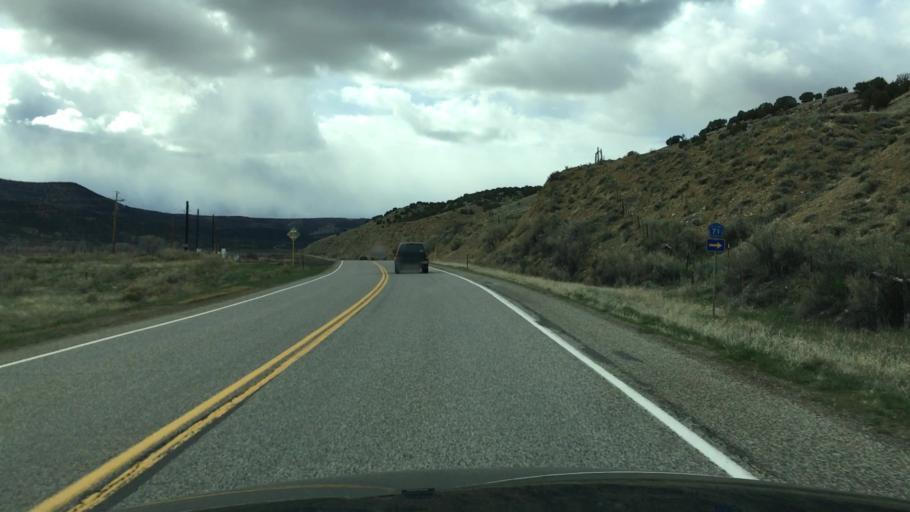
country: US
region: Colorado
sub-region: Rio Blanco County
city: Meeker
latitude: 40.0951
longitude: -108.2196
